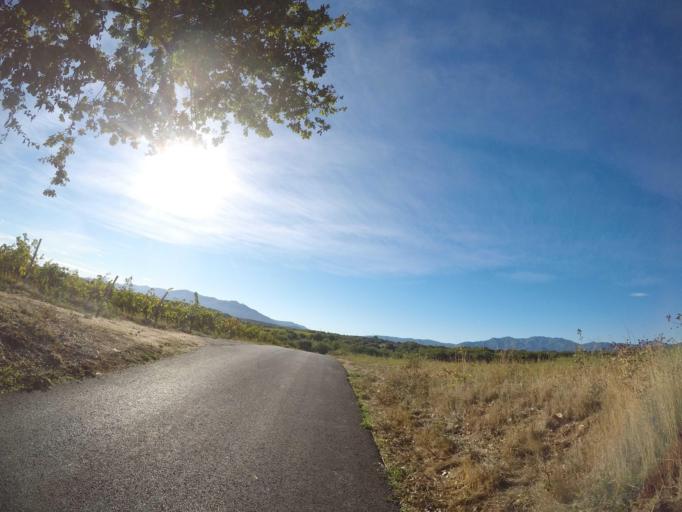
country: FR
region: Languedoc-Roussillon
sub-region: Departement des Pyrenees-Orientales
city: Trouillas
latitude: 42.5774
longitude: 2.7856
